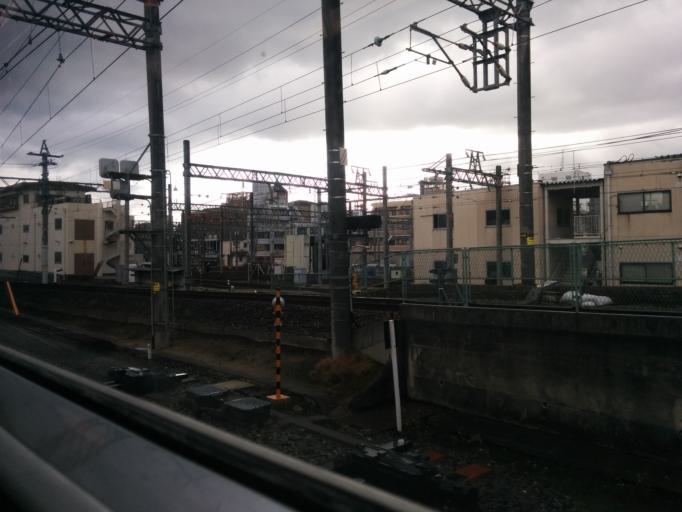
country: JP
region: Kyoto
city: Muko
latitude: 34.9814
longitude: 135.7034
